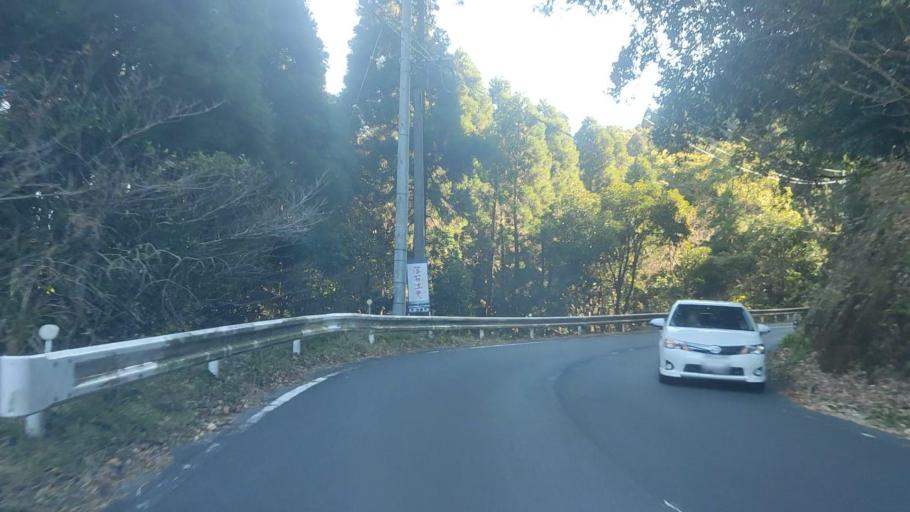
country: JP
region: Kagoshima
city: Kokubu-matsuki
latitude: 31.6706
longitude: 130.8334
